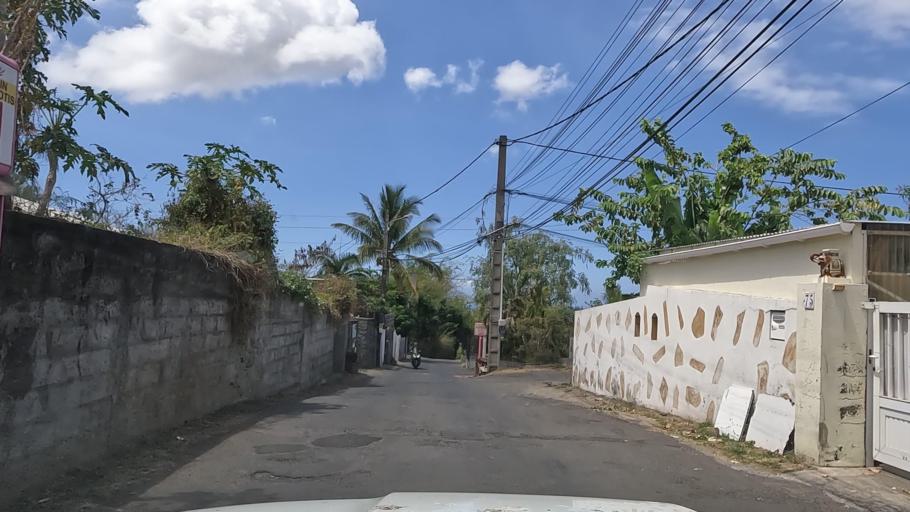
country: RE
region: Reunion
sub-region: Reunion
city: Saint-Louis
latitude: -21.2781
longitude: 55.4452
